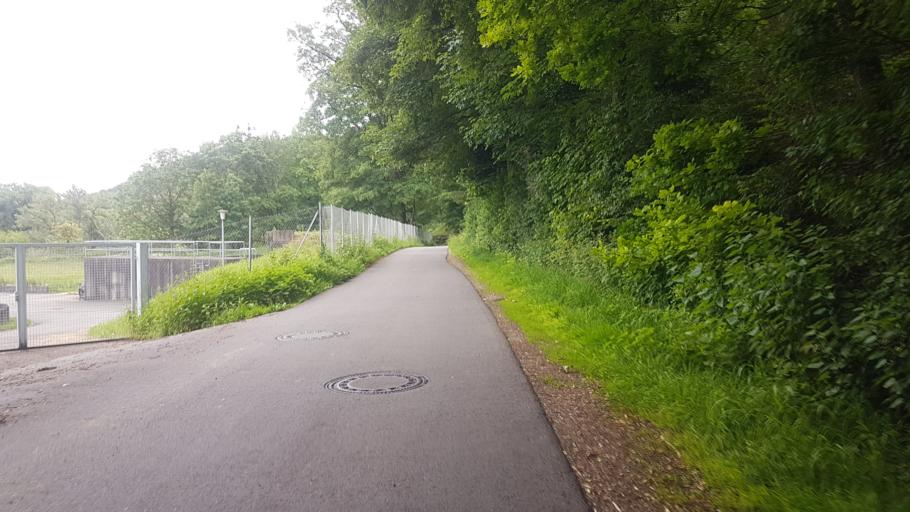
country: DE
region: Baden-Wuerttemberg
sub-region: Tuebingen Region
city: Sigmaringen
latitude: 48.0772
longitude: 9.2269
